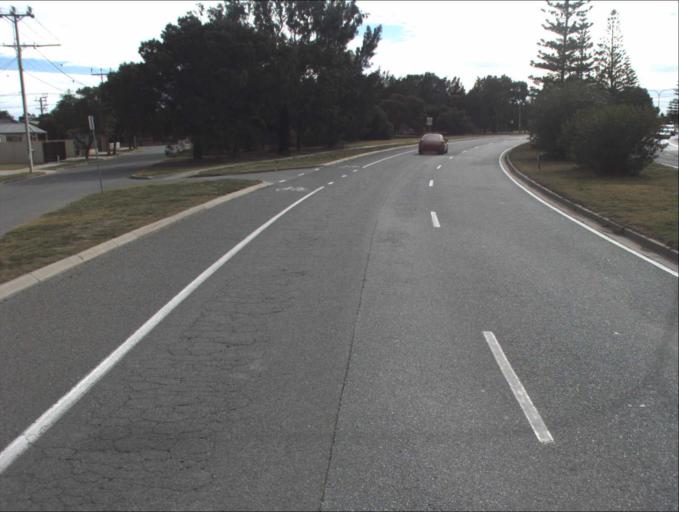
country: AU
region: South Australia
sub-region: Port Adelaide Enfield
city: Birkenhead
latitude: -34.8232
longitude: 138.4996
